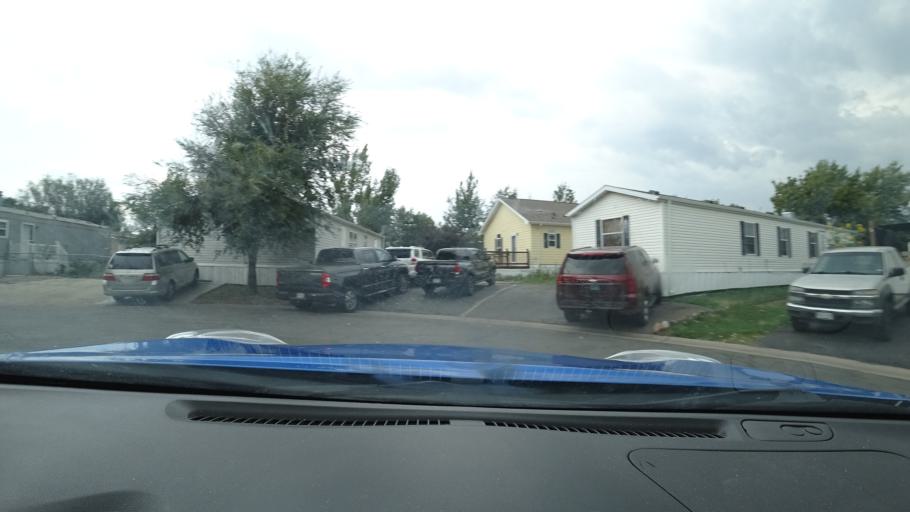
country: US
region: Colorado
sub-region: Adams County
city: Aurora
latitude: 39.7424
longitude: -104.7856
